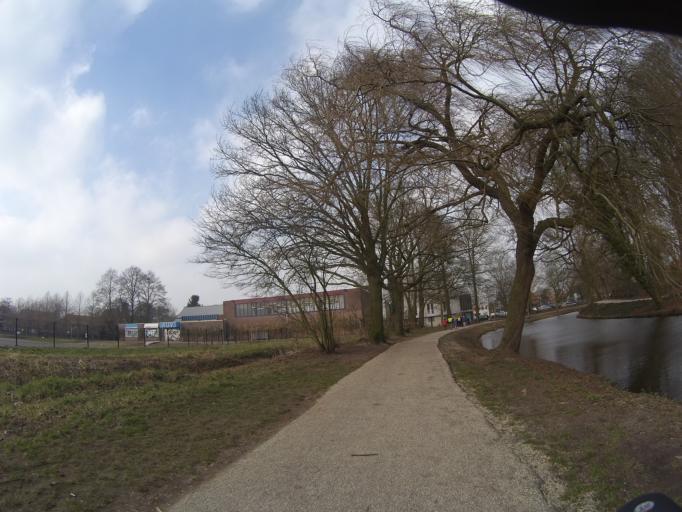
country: NL
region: Utrecht
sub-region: Gemeente Amersfoort
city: Randenbroek
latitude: 52.1501
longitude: 5.3954
